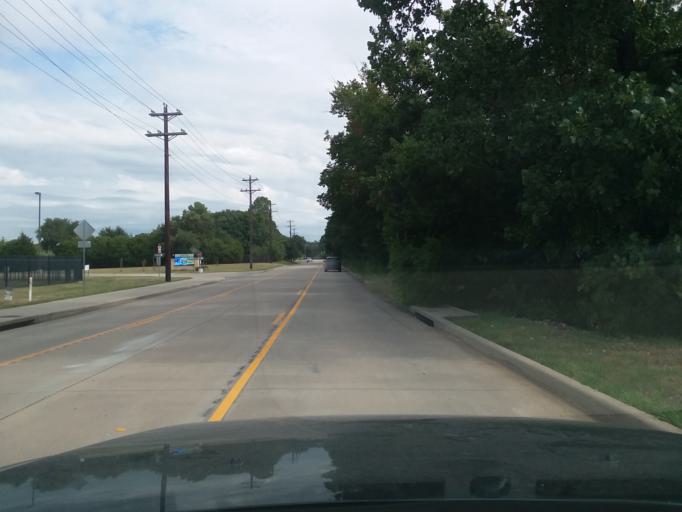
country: US
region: Texas
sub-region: Denton County
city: Copper Canyon
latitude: 33.1138
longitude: -97.1223
